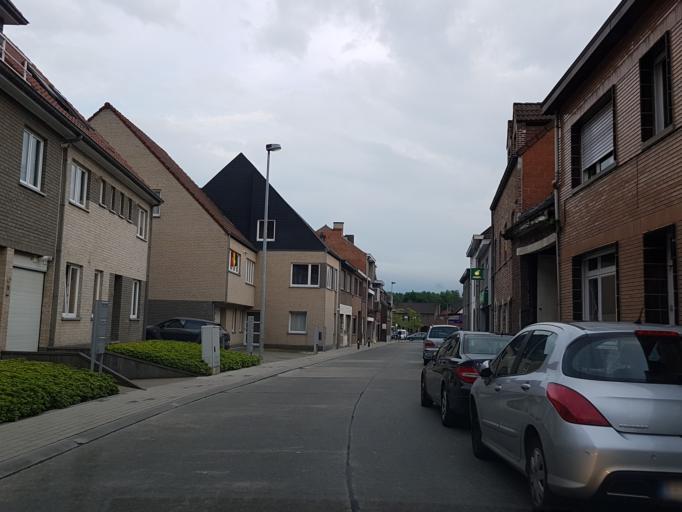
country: BE
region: Flanders
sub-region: Provincie Vlaams-Brabant
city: Liedekerke
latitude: 50.8897
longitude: 4.1007
